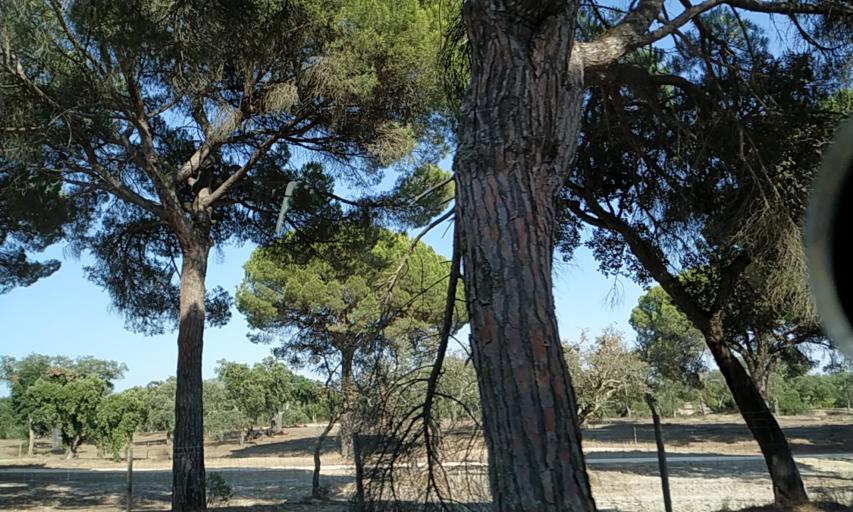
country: PT
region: Santarem
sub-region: Coruche
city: Coruche
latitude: 38.8070
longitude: -8.5787
